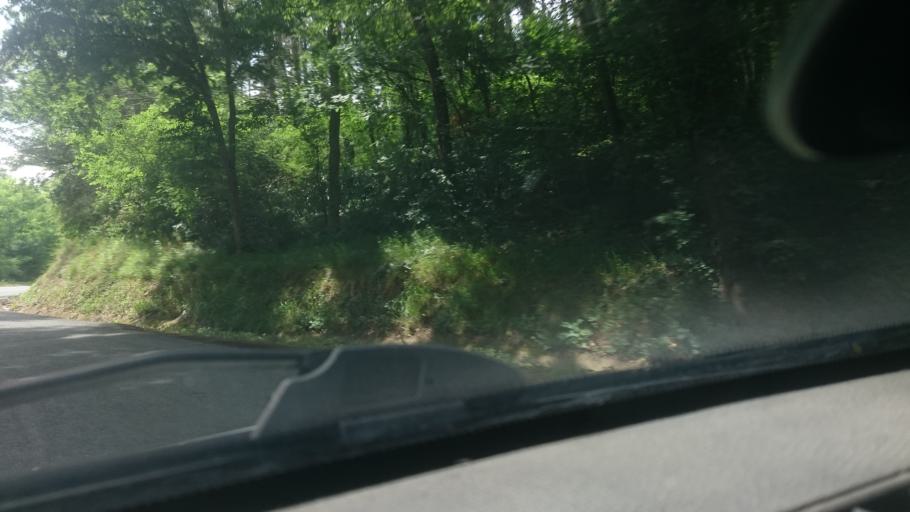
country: FR
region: Rhone-Alpes
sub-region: Departement du Rhone
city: Saint-Germain-Nuelles
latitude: 45.8516
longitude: 4.6448
